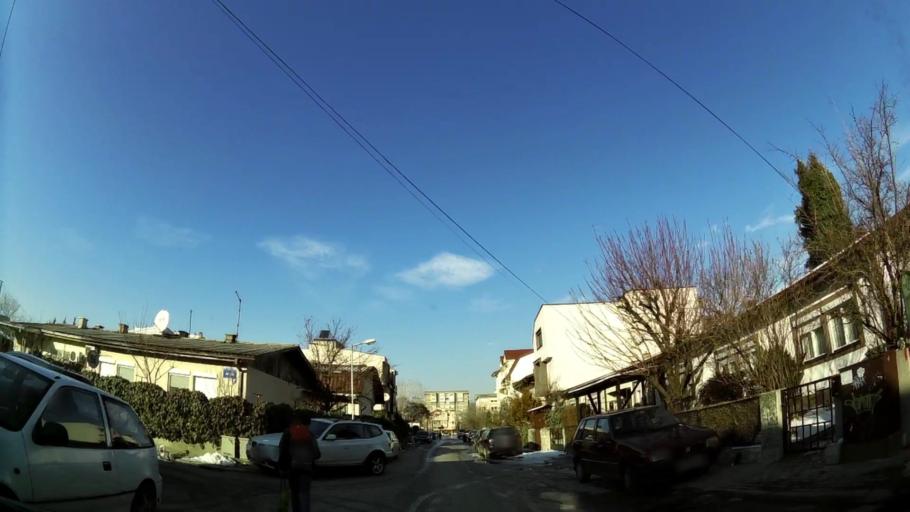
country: MK
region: Karpos
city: Skopje
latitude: 41.9995
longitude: 21.3945
